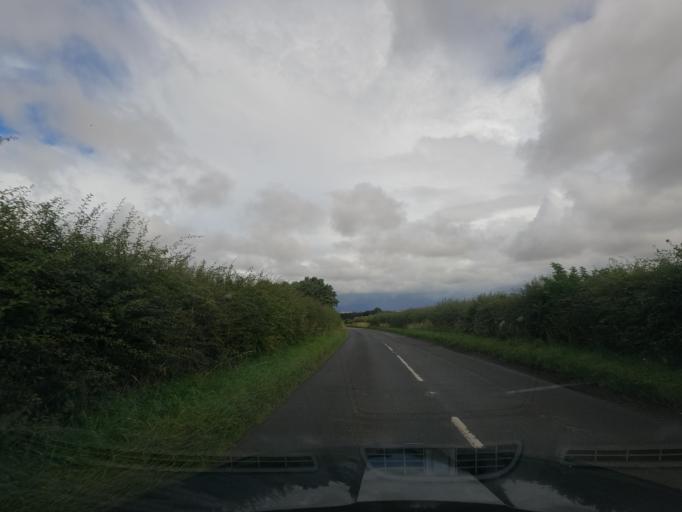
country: GB
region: England
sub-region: Northumberland
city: Lowick
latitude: 55.6571
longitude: -1.9957
